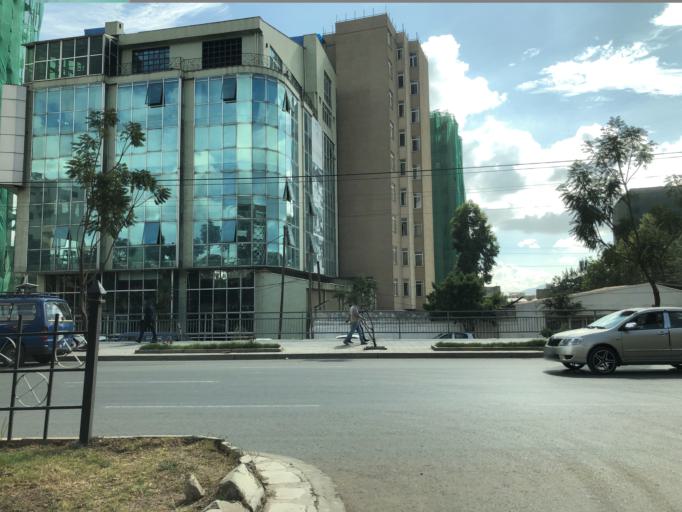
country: ET
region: Adis Abeba
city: Addis Ababa
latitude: 8.9909
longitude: 38.7840
